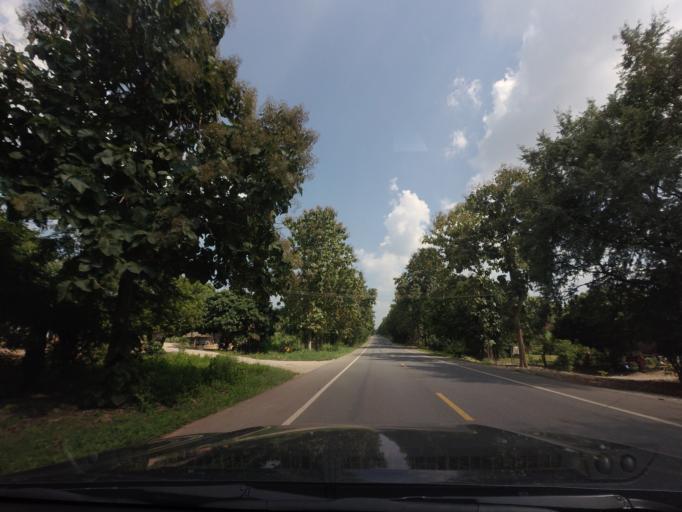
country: TH
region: Phitsanulok
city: Chat Trakan
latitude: 17.2849
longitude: 100.5242
